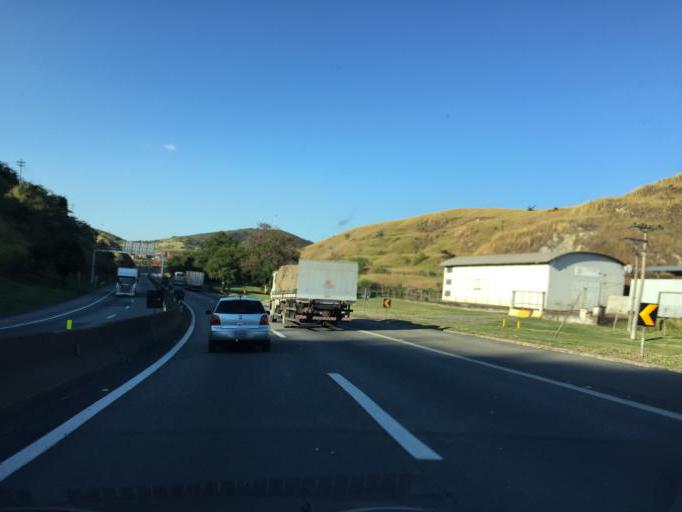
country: BR
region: Rio de Janeiro
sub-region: Barra Mansa
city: Barra Mansa
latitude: -22.5608
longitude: -44.1377
